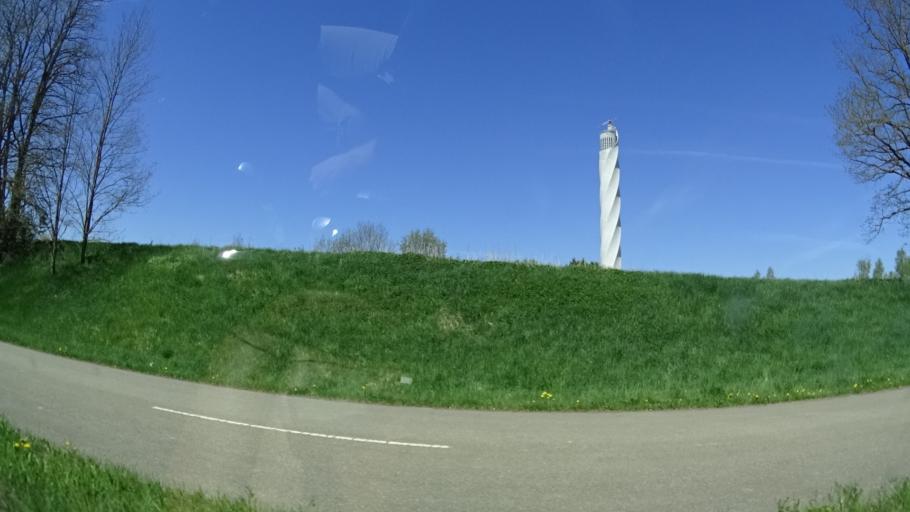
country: DE
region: Baden-Wuerttemberg
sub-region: Freiburg Region
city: Rottweil
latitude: 48.1756
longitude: 8.6317
